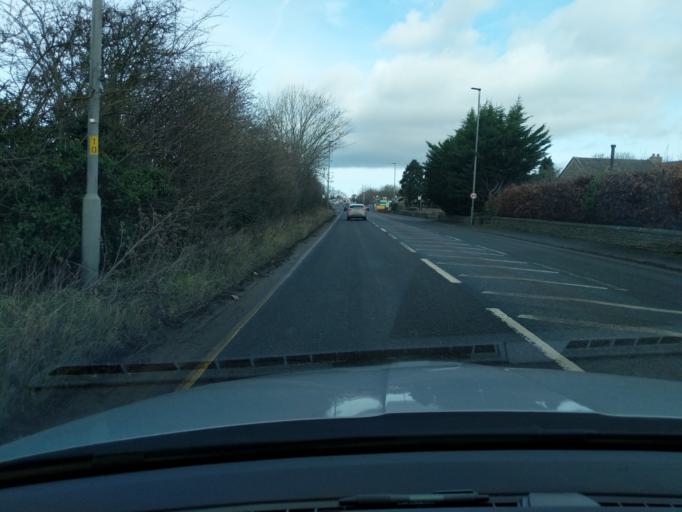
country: GB
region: England
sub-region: North Yorkshire
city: Catterick
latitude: 54.3901
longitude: -1.6519
